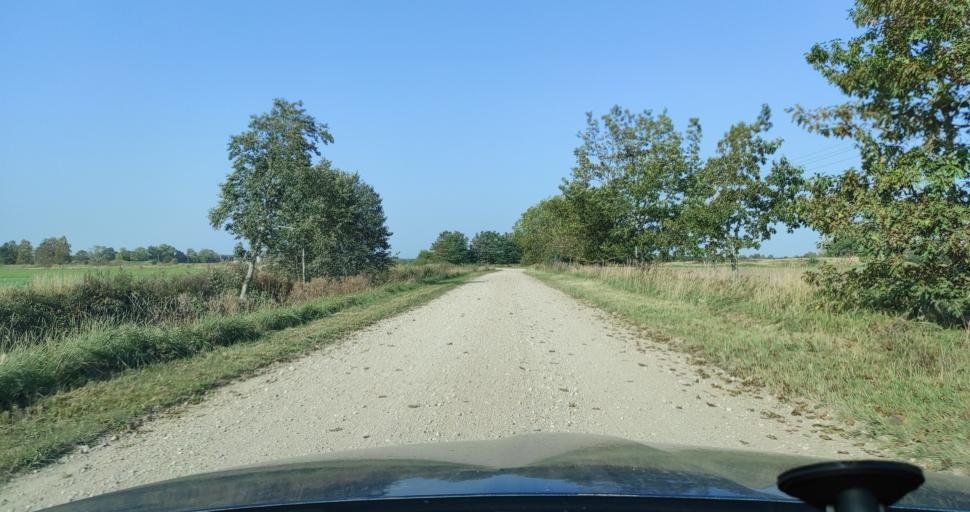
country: LV
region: Ventspils Rajons
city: Piltene
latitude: 57.2319
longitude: 21.6115
